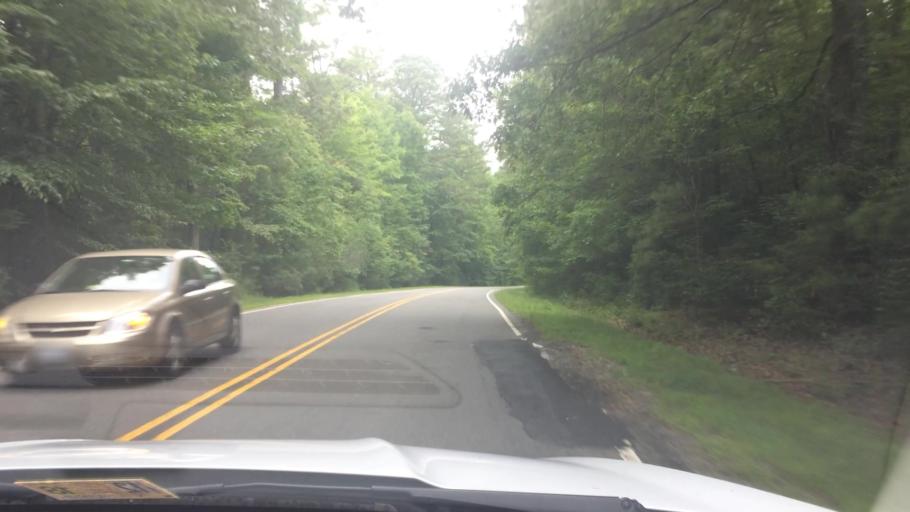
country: US
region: Virginia
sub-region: York County
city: Yorktown
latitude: 37.2304
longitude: -76.5291
